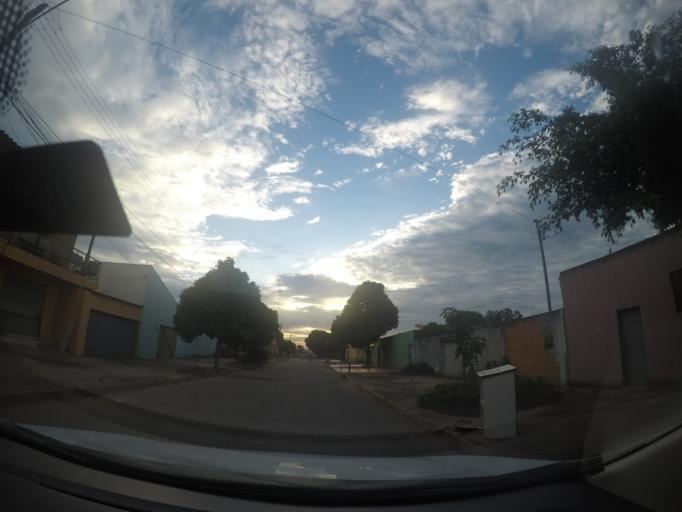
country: BR
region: Goias
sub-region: Goiania
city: Goiania
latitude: -16.6903
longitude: -49.3473
